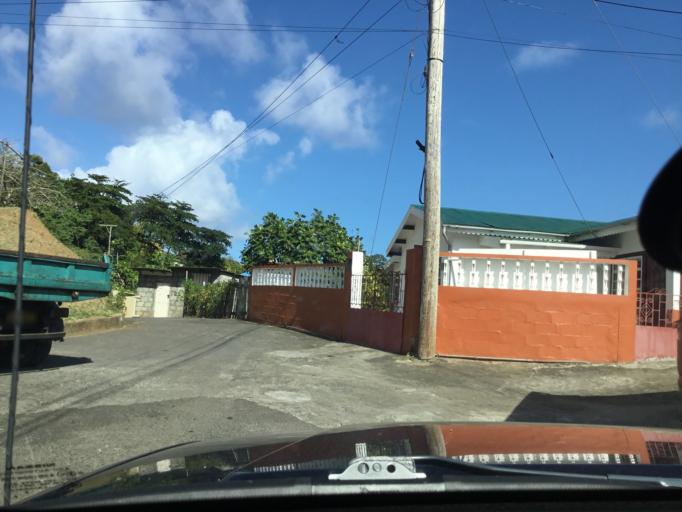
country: VC
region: Charlotte
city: Biabou
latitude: 13.1608
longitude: -61.1668
